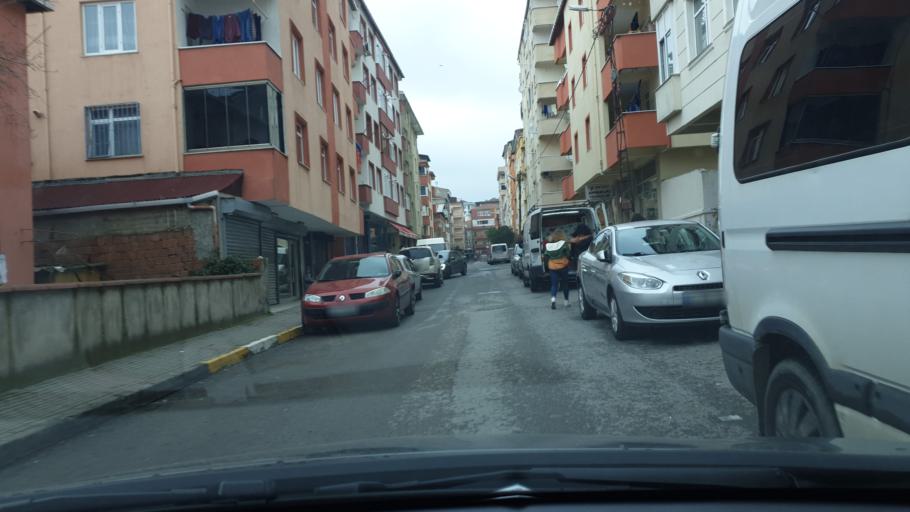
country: TR
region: Istanbul
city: Pendik
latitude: 40.8798
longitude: 29.2717
